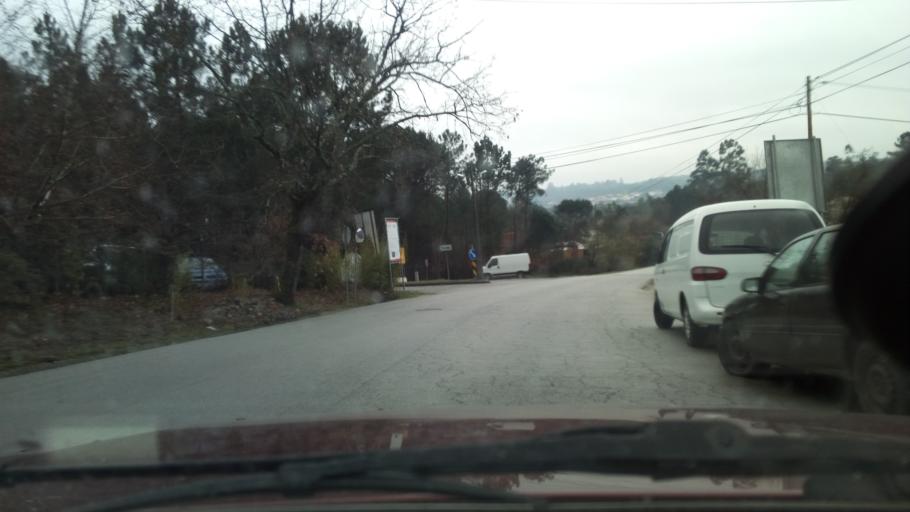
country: PT
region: Viseu
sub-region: Mangualde
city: Mangualde
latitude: 40.6189
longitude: -7.7964
